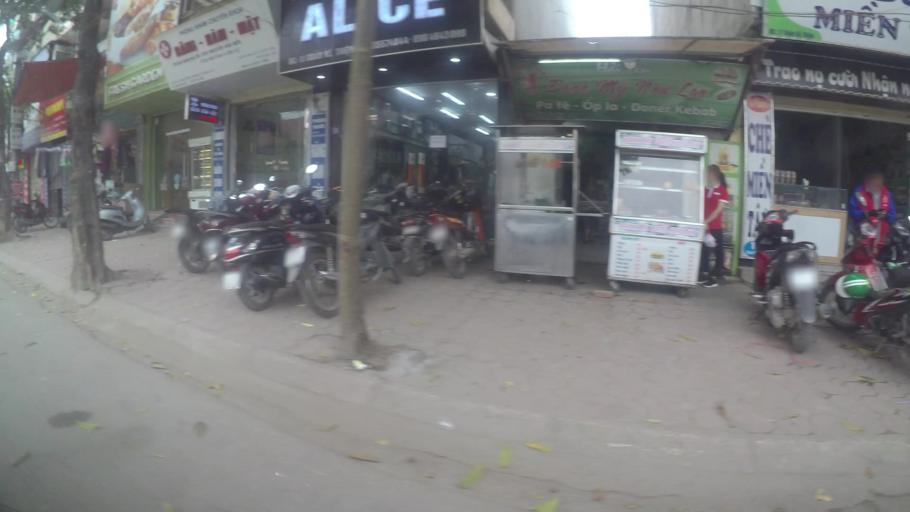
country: VN
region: Ha Noi
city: Cau Dien
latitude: 21.0409
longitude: 105.7798
